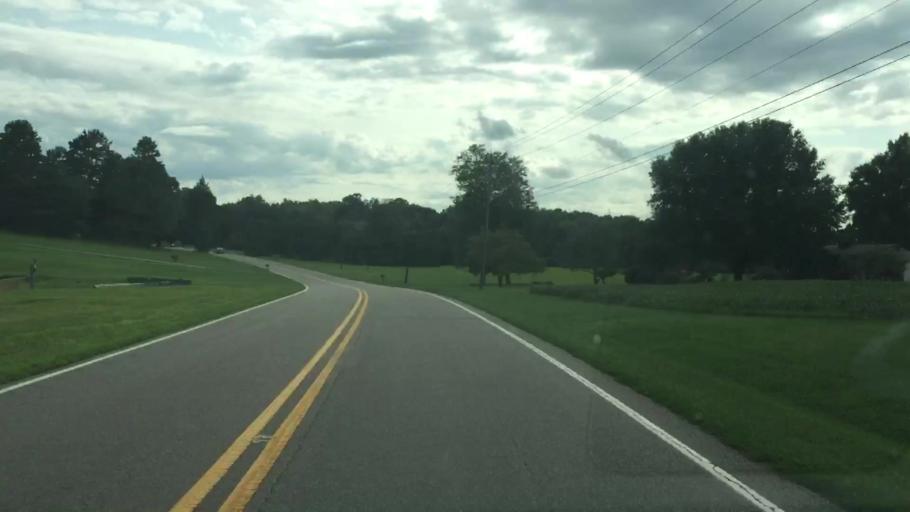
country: US
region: North Carolina
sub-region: Iredell County
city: Mooresville
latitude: 35.6140
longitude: -80.7395
